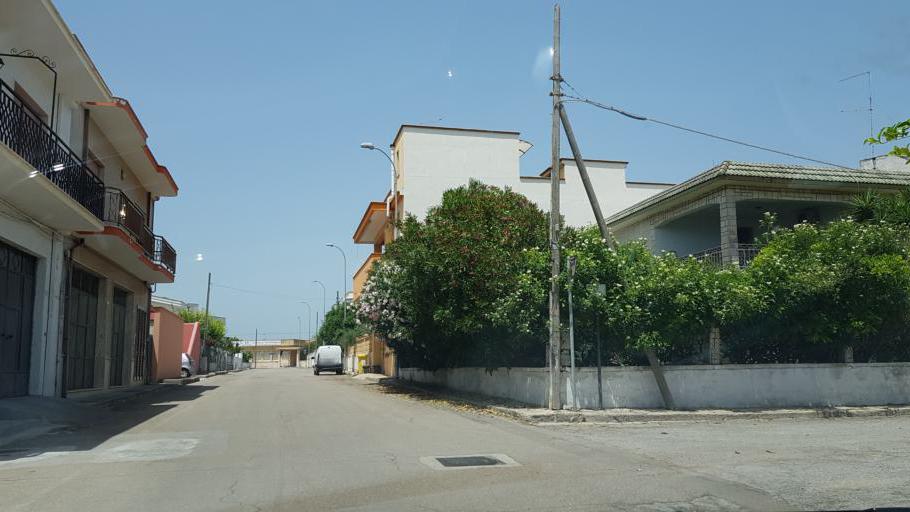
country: IT
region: Apulia
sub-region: Provincia di Brindisi
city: San Pancrazio Salentino
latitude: 40.4217
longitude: 17.8470
